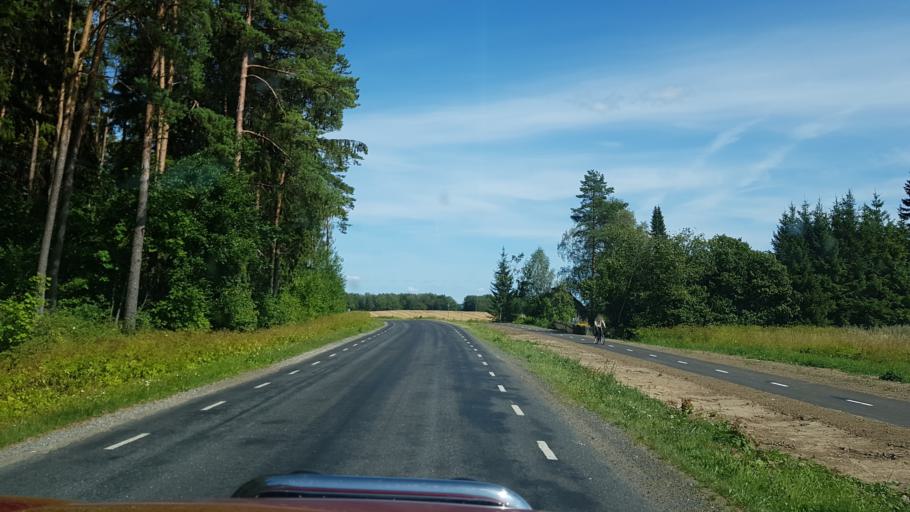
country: EE
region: Jaervamaa
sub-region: Jaerva-Jaani vald
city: Jarva-Jaani
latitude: 59.0382
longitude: 25.9334
